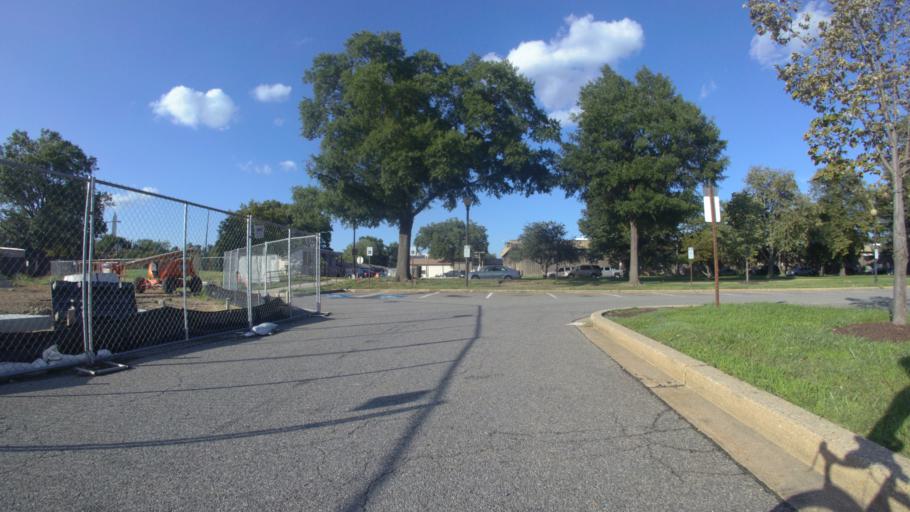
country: US
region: Washington, D.C.
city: Washington, D.C.
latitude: 38.8774
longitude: -77.0341
